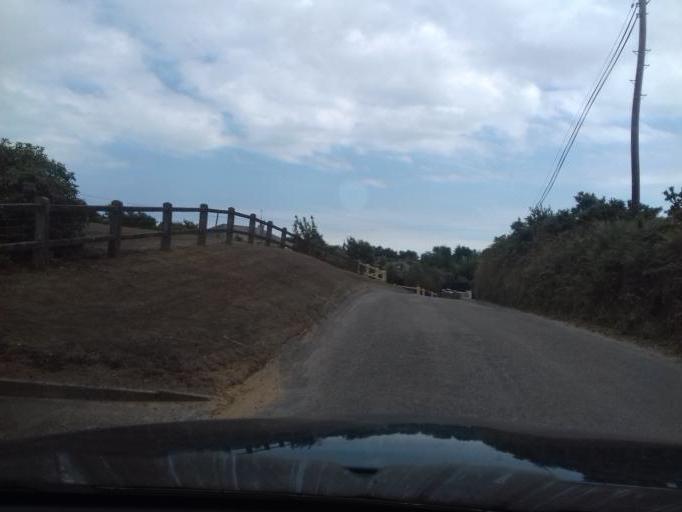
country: IE
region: Leinster
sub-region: Loch Garman
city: Castlebridge
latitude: 52.4026
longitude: -6.4036
